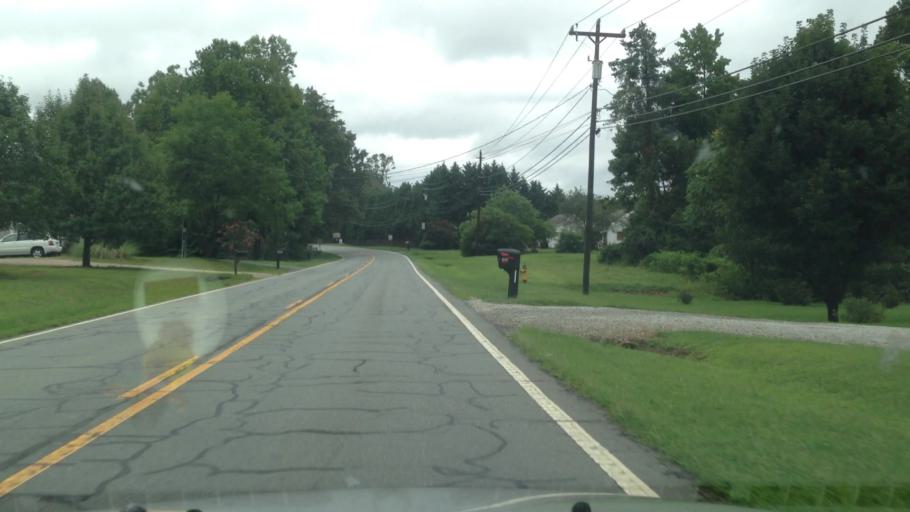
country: US
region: North Carolina
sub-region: Forsyth County
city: Kernersville
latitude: 36.1714
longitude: -80.0579
